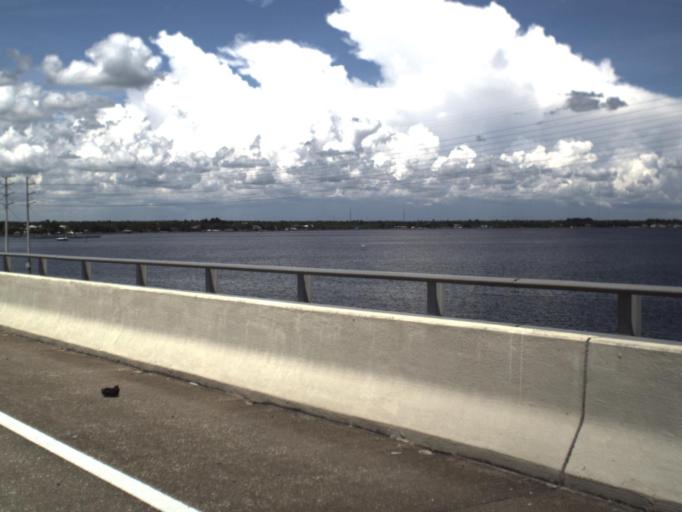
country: US
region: Florida
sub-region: Charlotte County
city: Charlotte Harbor
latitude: 26.9456
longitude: -82.0572
